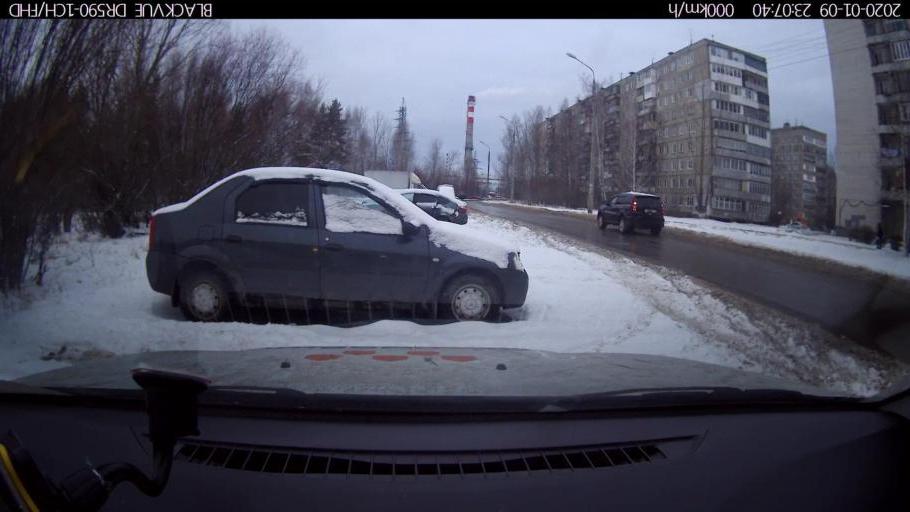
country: RU
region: Nizjnij Novgorod
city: Gorbatovka
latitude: 56.3680
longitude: 43.8004
